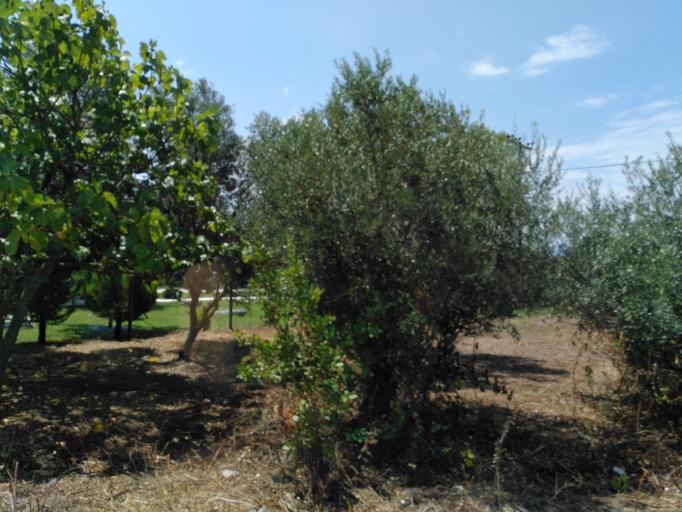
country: GR
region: Central Macedonia
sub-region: Nomos Thessalonikis
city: Agia Triada
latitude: 40.4975
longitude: 22.8476
